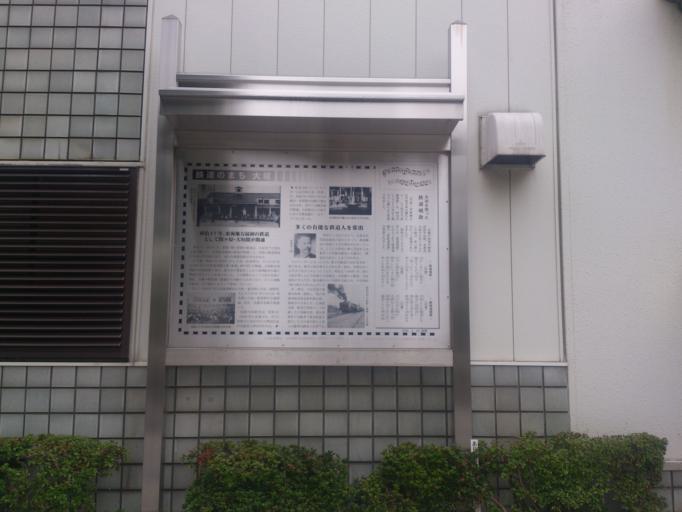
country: JP
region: Gifu
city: Ogaki
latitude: 35.3665
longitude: 136.6173
